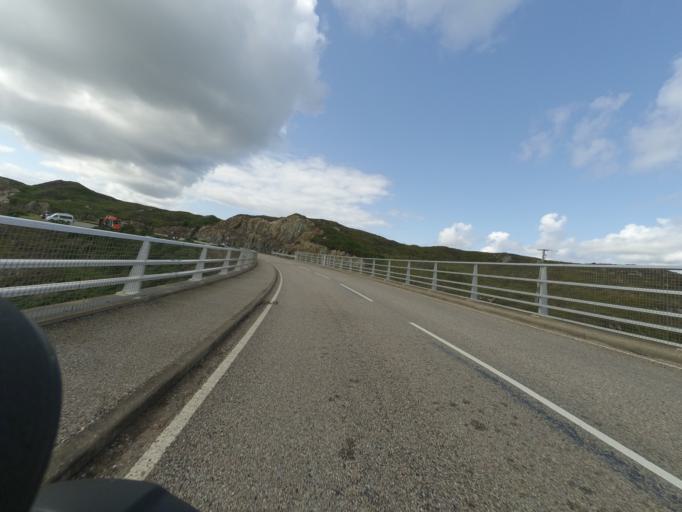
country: GB
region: Scotland
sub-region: Highland
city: Ullapool
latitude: 58.2577
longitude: -5.0251
